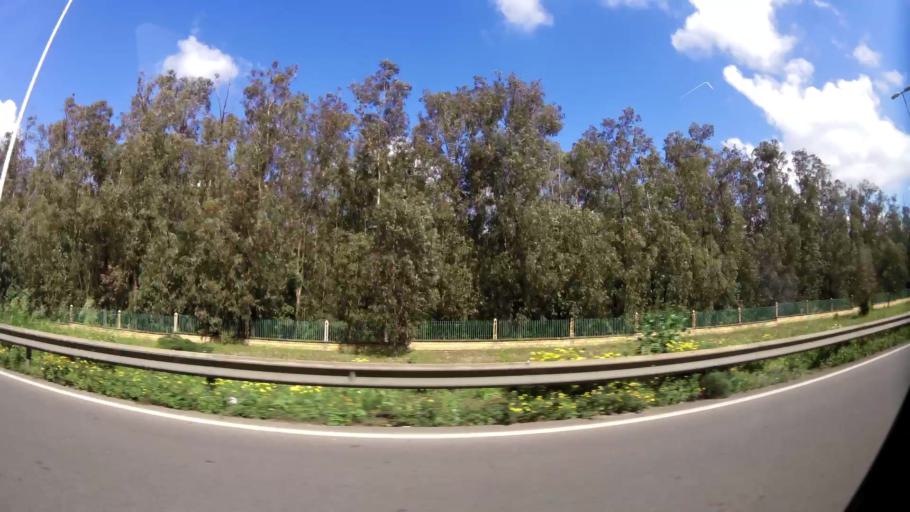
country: MA
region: Grand Casablanca
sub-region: Nouaceur
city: Bouskoura
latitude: 33.4728
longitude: -7.6335
